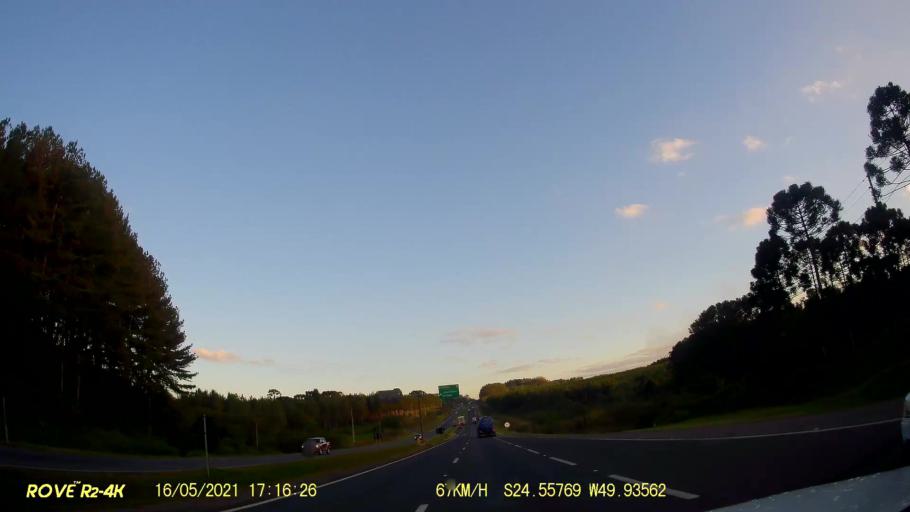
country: BR
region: Parana
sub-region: Pirai Do Sul
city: Pirai do Sul
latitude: -24.5579
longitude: -49.9356
